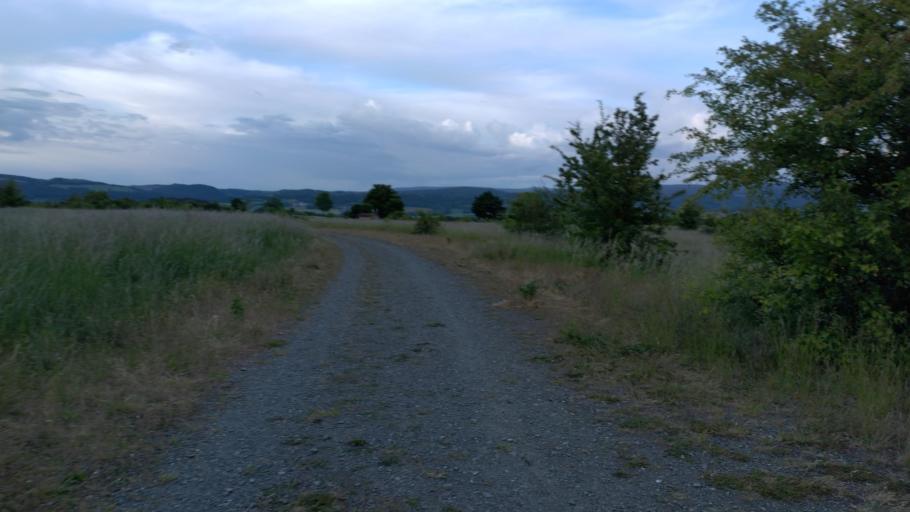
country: DE
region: Bavaria
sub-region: Upper Franconia
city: Bindlach
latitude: 49.9972
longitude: 11.6213
